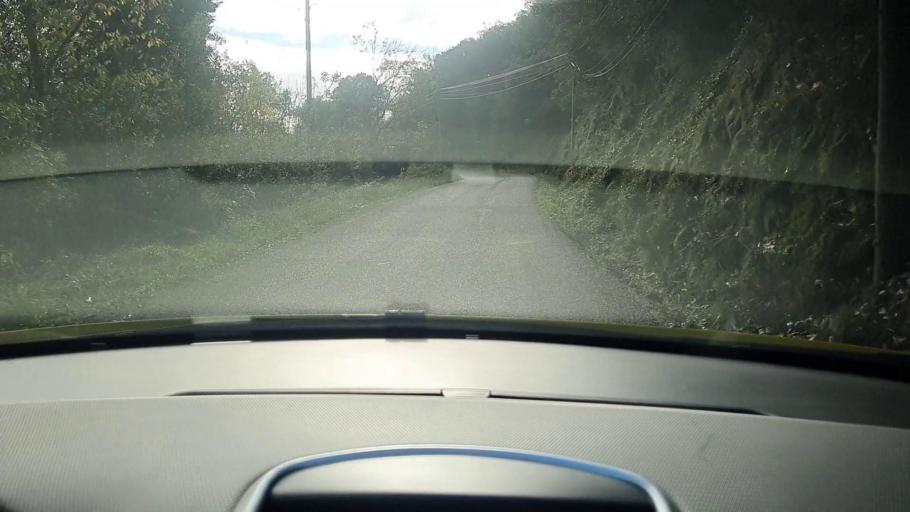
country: FR
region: Languedoc-Roussillon
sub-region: Departement du Gard
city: Lasalle
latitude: 44.0697
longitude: 3.8311
